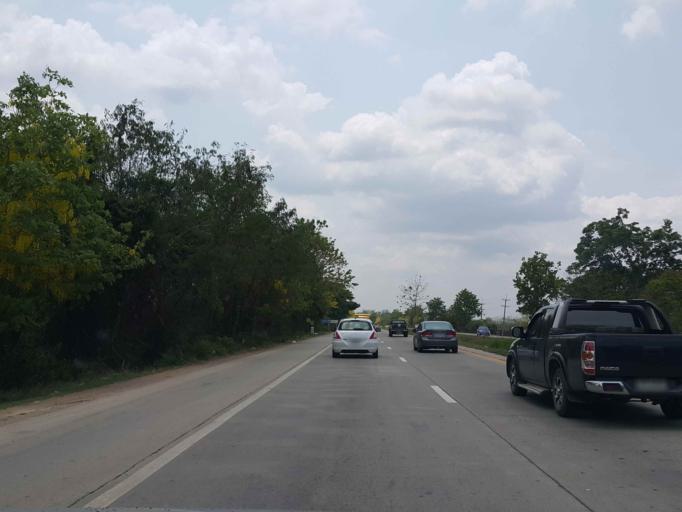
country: TH
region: Lampang
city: Ko Kha
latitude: 18.2362
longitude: 99.4368
